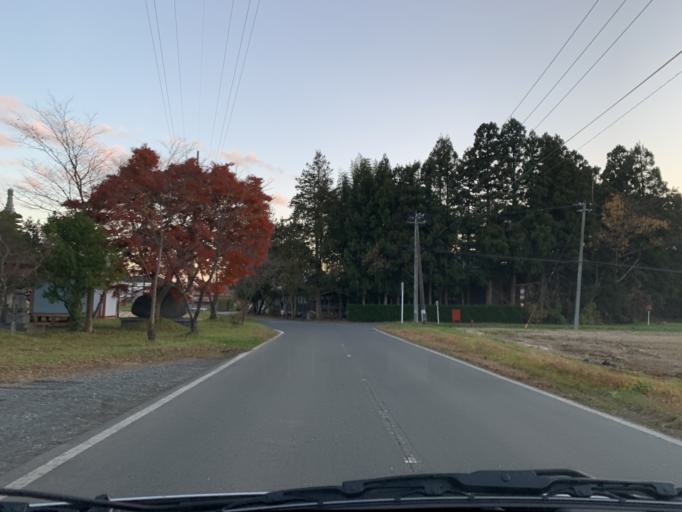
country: JP
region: Iwate
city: Ichinoseki
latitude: 39.0103
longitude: 141.1076
